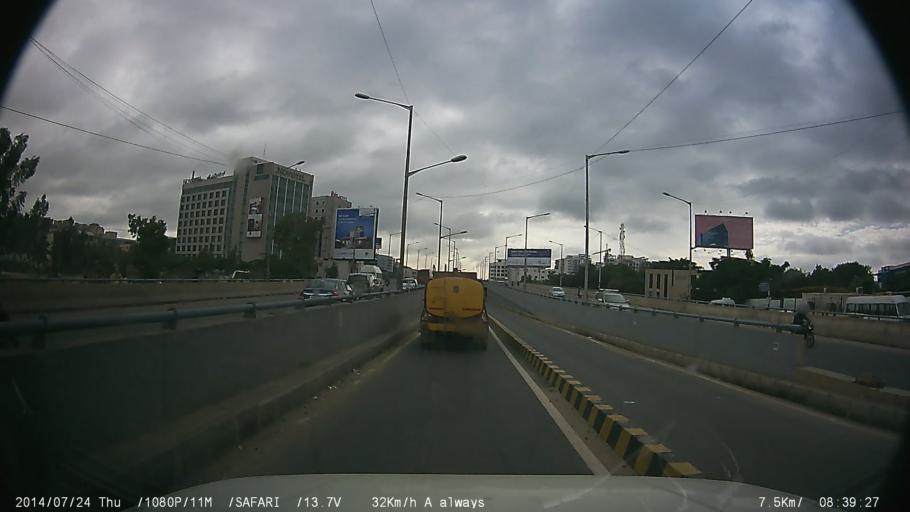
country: IN
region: Karnataka
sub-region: Bangalore Urban
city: Bangalore
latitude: 12.9285
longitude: 77.6818
